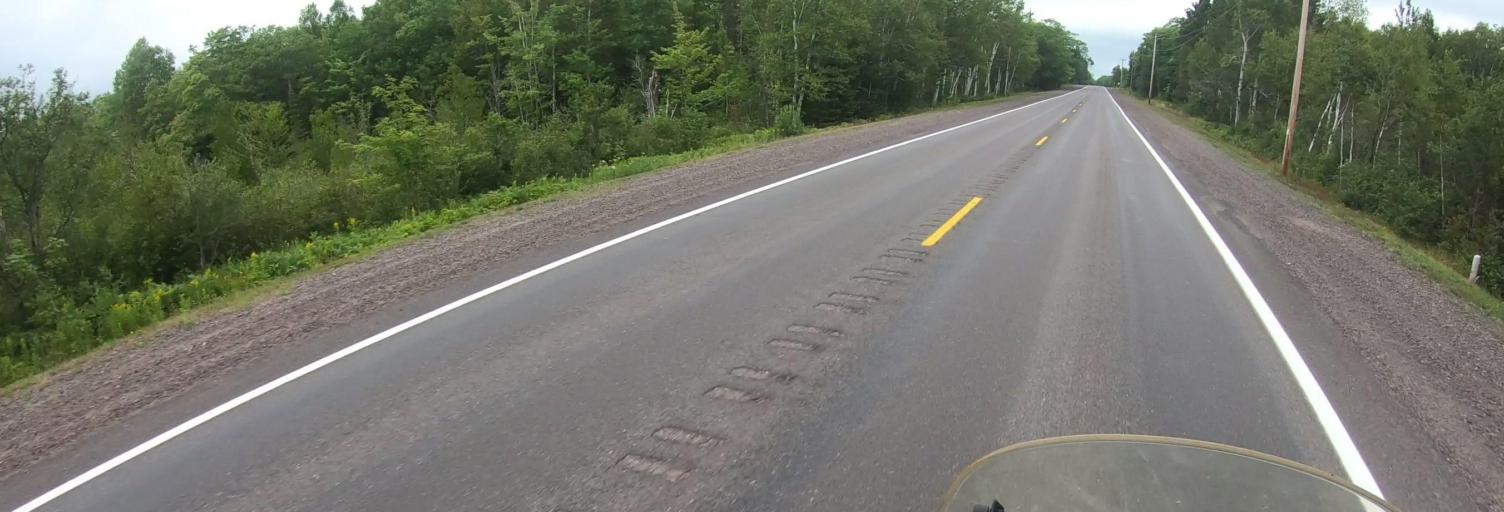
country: US
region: Michigan
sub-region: Keweenaw County
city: Eagle River
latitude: 47.3132
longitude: -88.3515
